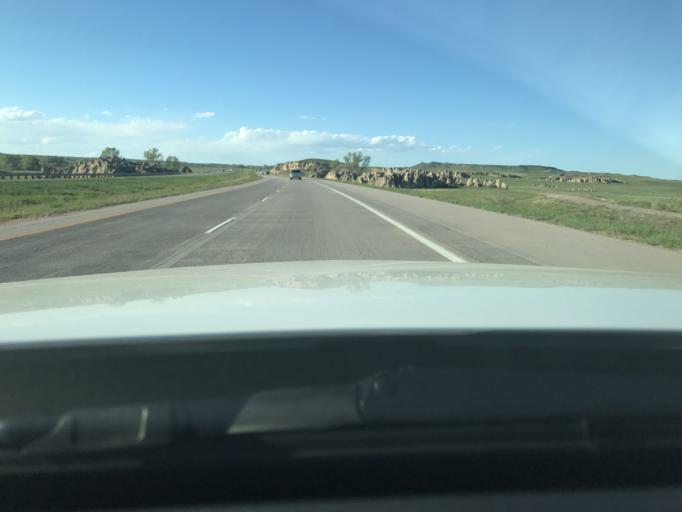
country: US
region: Wyoming
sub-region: Laramie County
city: South Greeley
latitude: 40.9509
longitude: -104.9241
